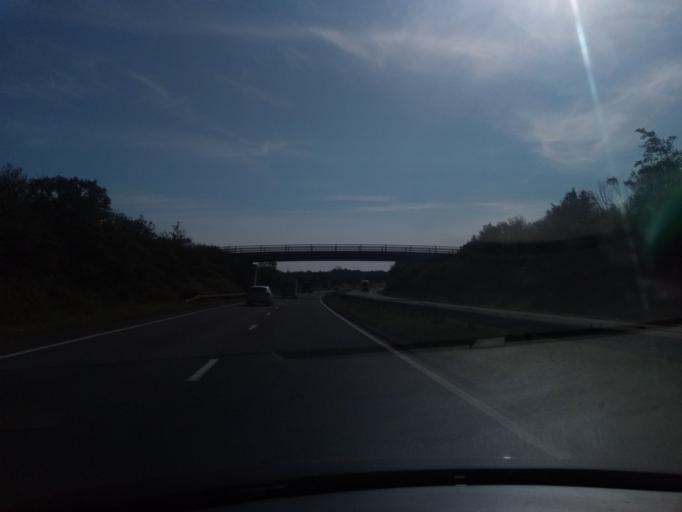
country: GB
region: England
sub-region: Sunderland
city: Ryhope
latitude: 54.8464
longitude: -1.3801
